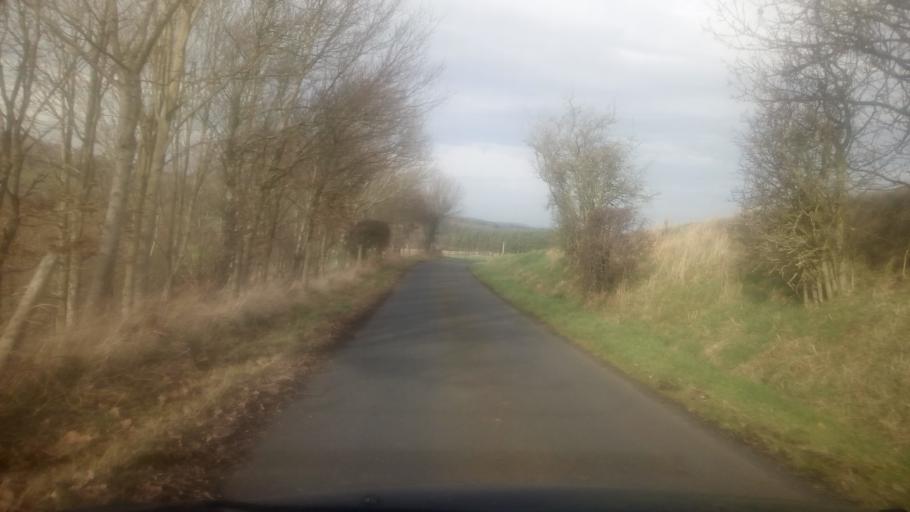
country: GB
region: Scotland
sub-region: The Scottish Borders
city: Jedburgh
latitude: 55.4295
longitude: -2.6250
